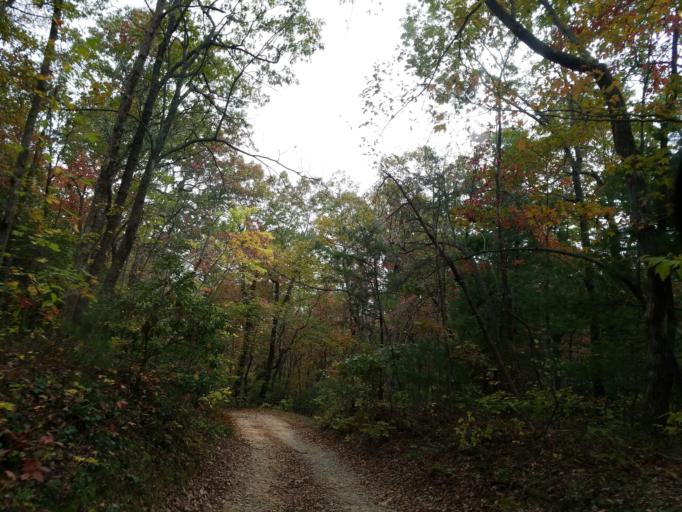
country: US
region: Georgia
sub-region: Dawson County
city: Dawsonville
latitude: 34.5893
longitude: -84.2294
